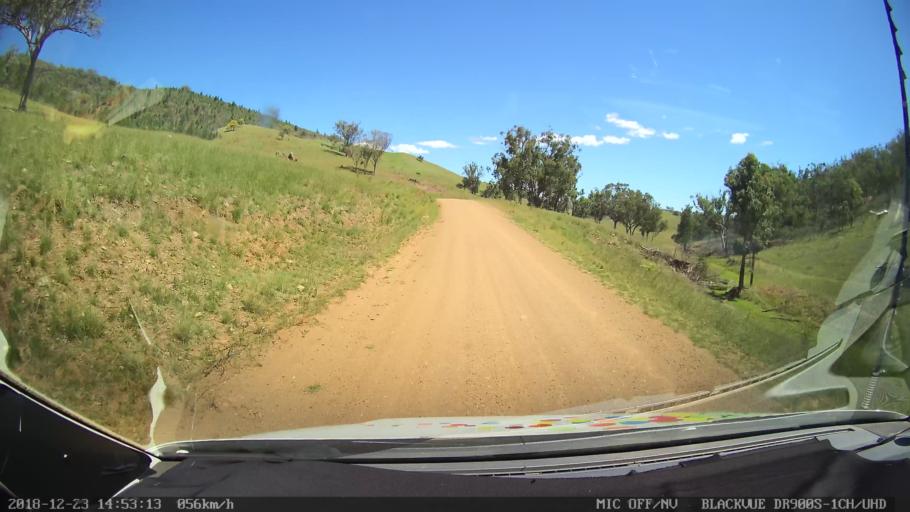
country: AU
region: New South Wales
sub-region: Tamworth Municipality
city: Manilla
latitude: -30.6899
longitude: 150.8518
